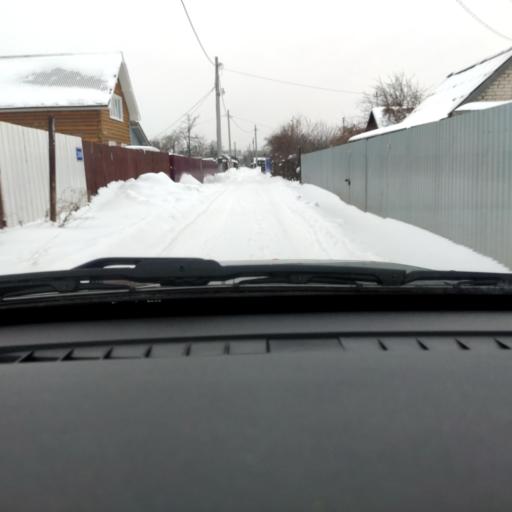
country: RU
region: Samara
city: Tol'yatti
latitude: 53.5414
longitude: 49.4350
